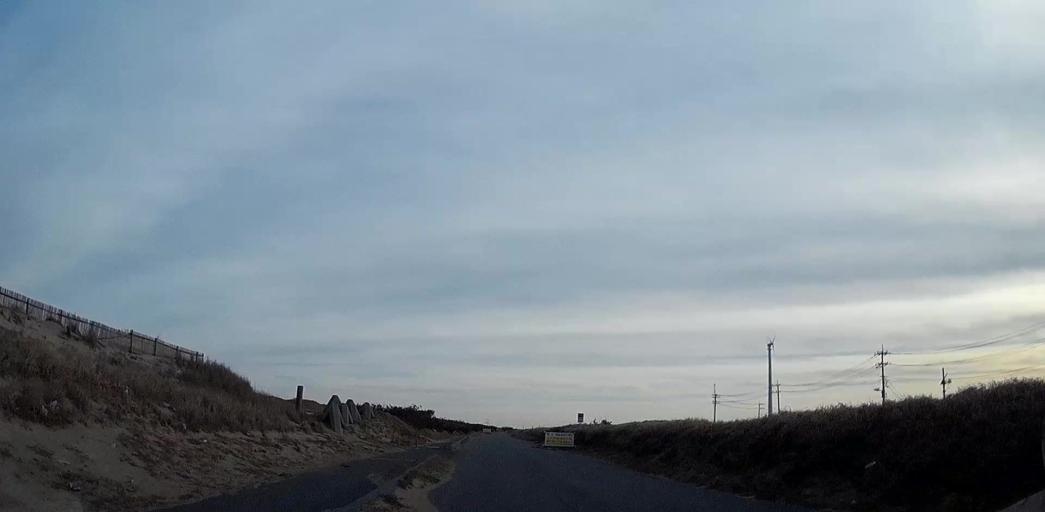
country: JP
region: Chiba
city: Hasaki
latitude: 35.7862
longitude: 140.8023
